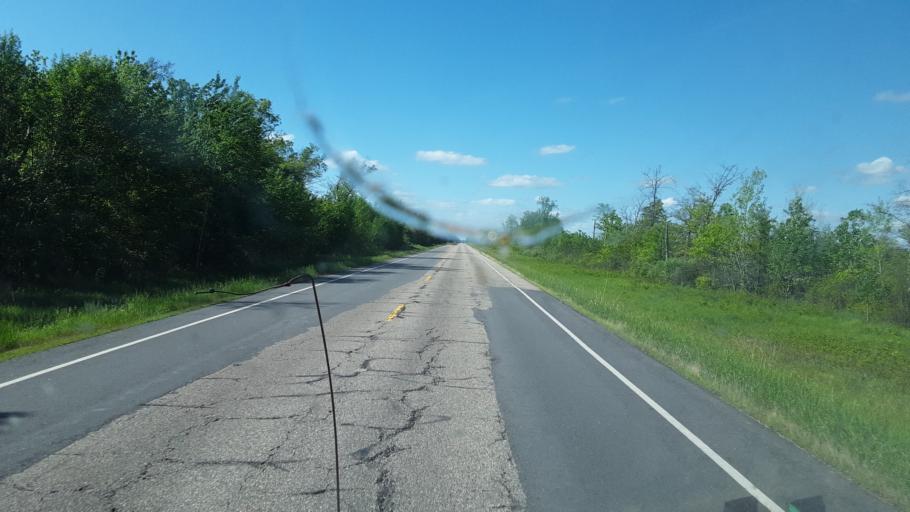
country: US
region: Wisconsin
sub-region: Wood County
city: Nekoosa
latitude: 44.1869
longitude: -90.1348
